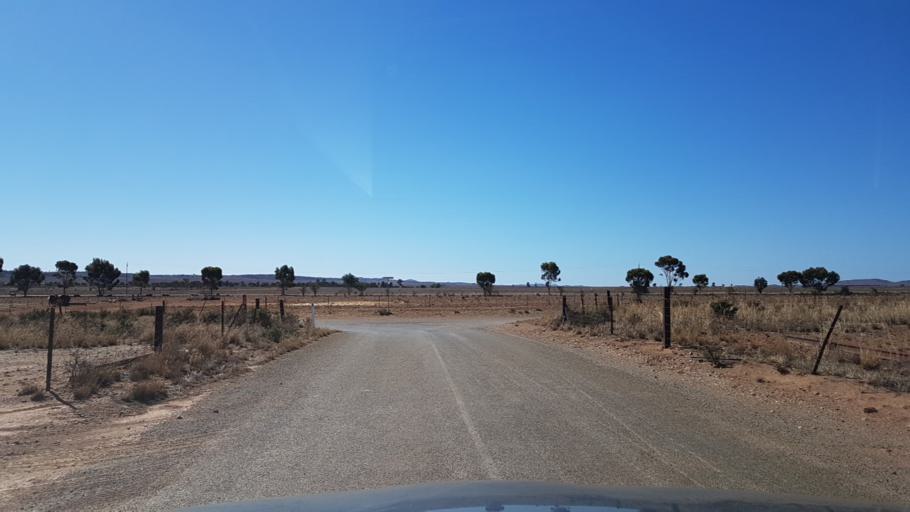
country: AU
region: South Australia
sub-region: Peterborough
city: Peterborough
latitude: -32.9718
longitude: 138.8585
